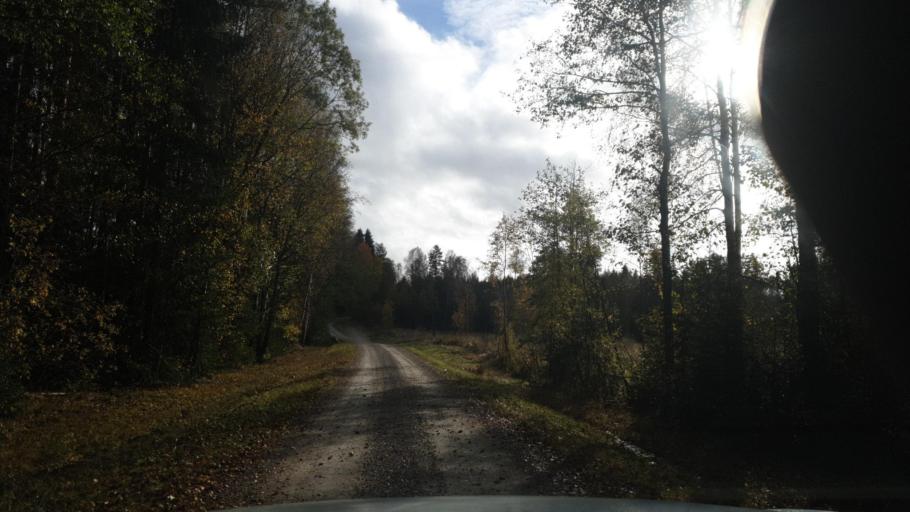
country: SE
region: Vaermland
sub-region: Karlstads Kommun
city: Edsvalla
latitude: 59.6101
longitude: 12.9831
